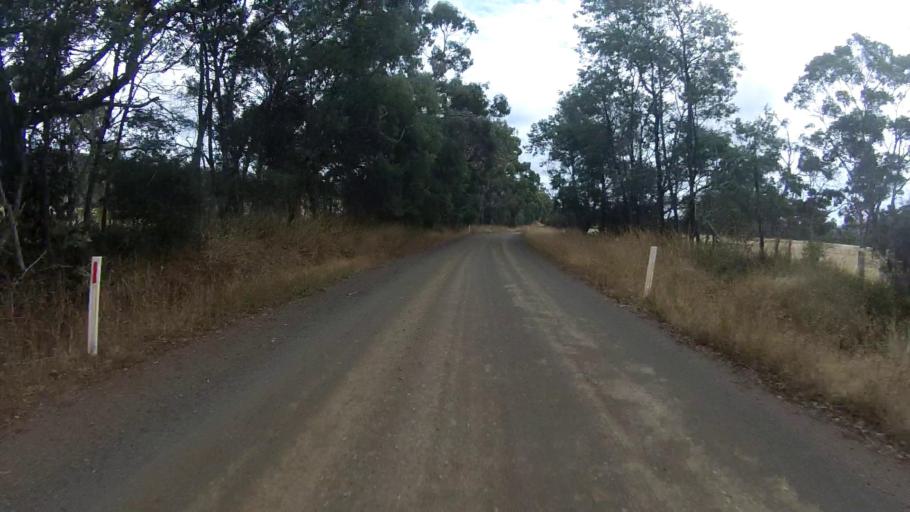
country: AU
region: Tasmania
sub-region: Break O'Day
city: St Helens
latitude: -41.8257
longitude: 147.9819
